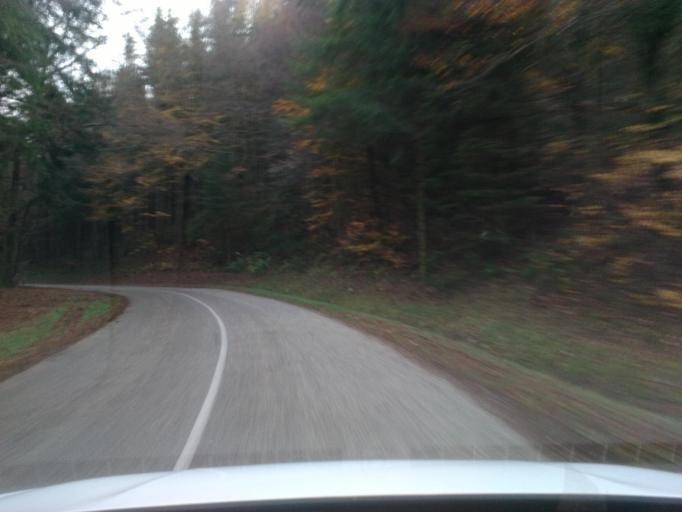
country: FR
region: Lorraine
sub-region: Departement des Vosges
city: Senones
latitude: 48.4015
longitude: 7.0896
